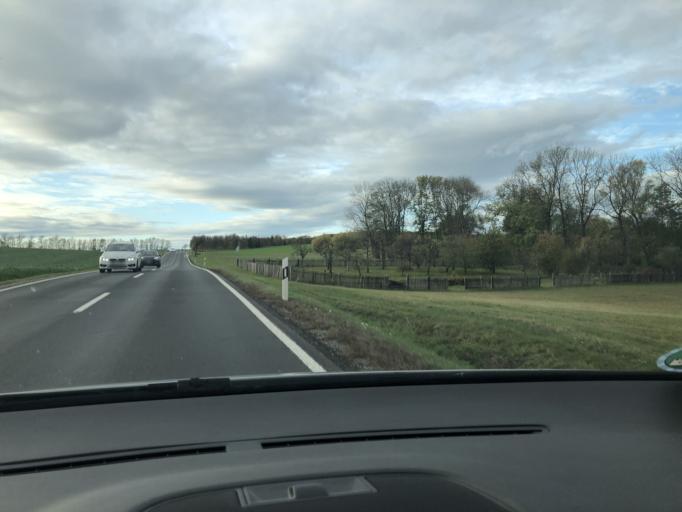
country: DE
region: Thuringia
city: Frankendorf
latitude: 50.9674
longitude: 11.4454
